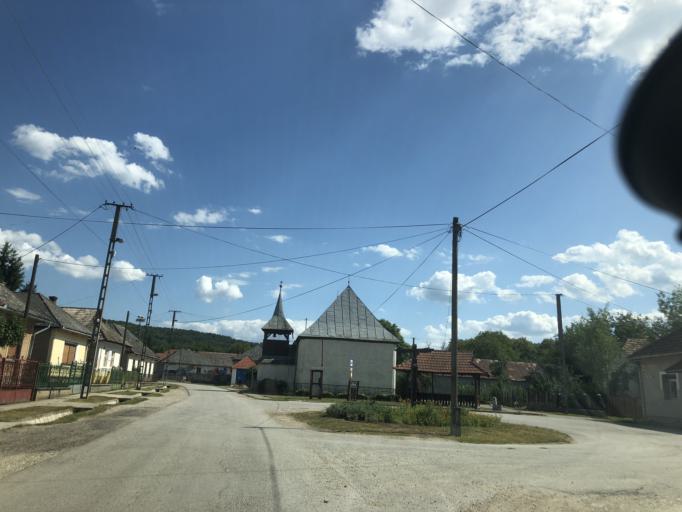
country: HU
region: Borsod-Abauj-Zemplen
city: Szendro
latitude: 48.5425
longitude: 20.8035
